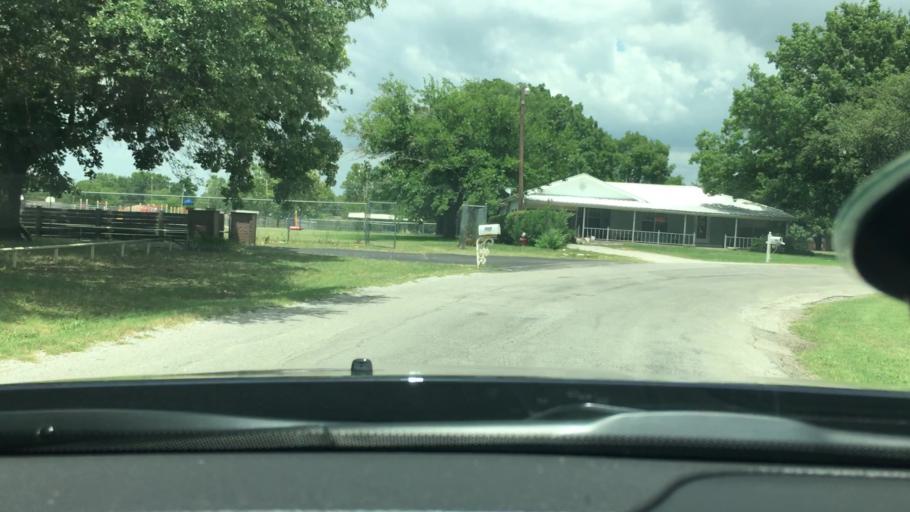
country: US
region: Oklahoma
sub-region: Love County
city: Marietta
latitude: 33.9292
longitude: -97.1220
